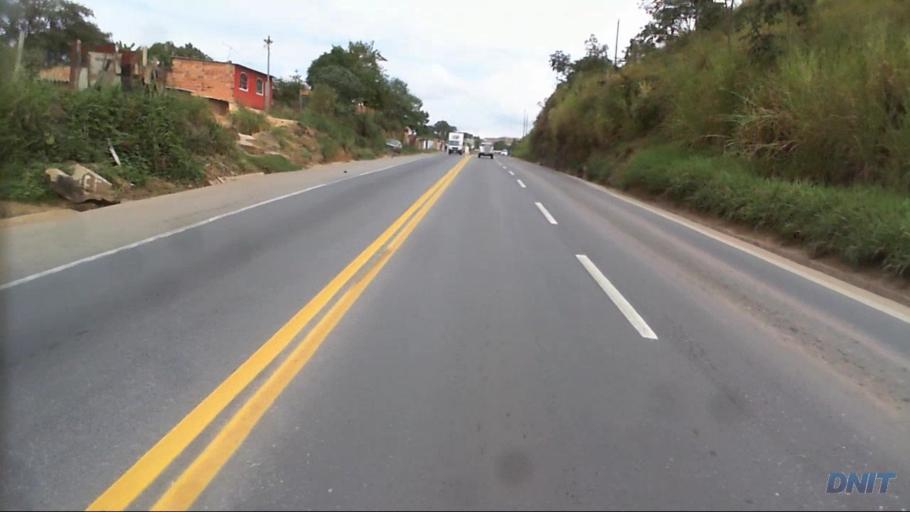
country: BR
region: Minas Gerais
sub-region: Santa Luzia
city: Santa Luzia
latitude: -19.8400
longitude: -43.8854
